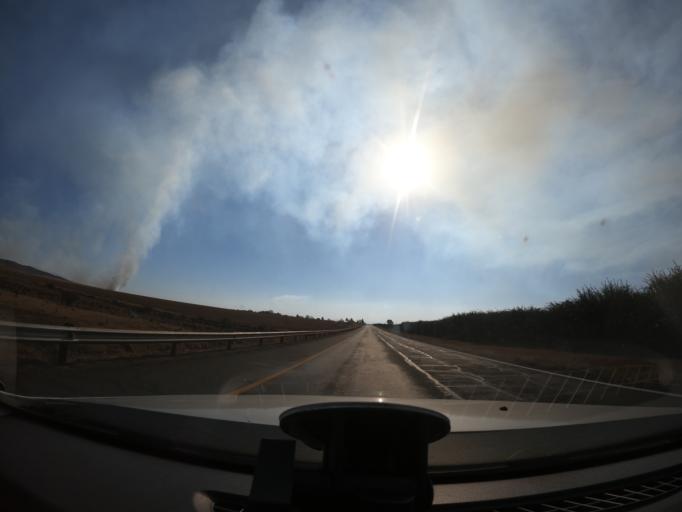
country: ZA
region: Gauteng
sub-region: Sedibeng District Municipality
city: Heidelberg
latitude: -26.4571
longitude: 28.3263
